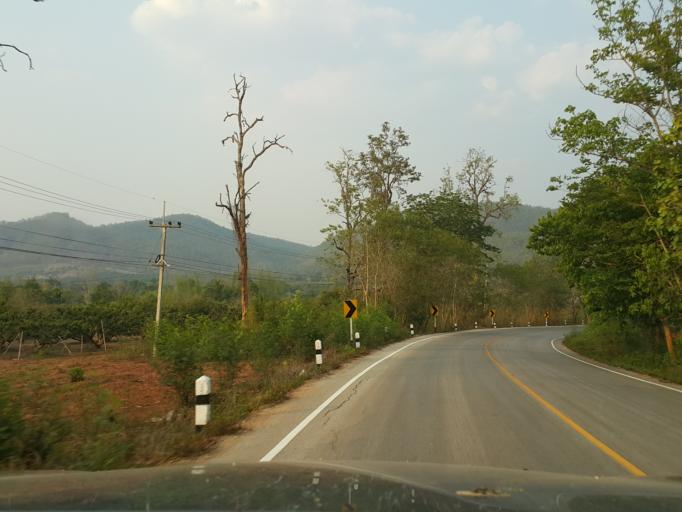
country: TH
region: Lamphun
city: Li
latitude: 17.8453
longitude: 98.9966
